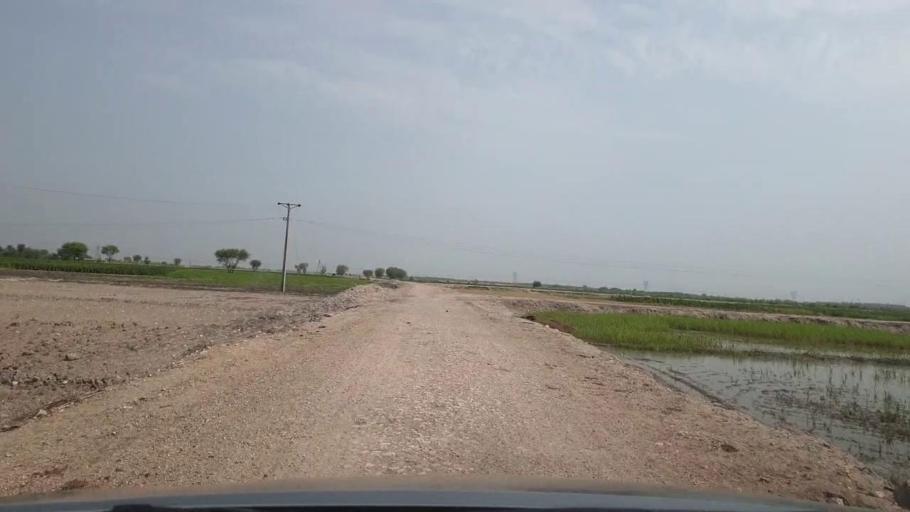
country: PK
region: Sindh
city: Rohri
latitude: 27.6613
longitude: 69.0257
